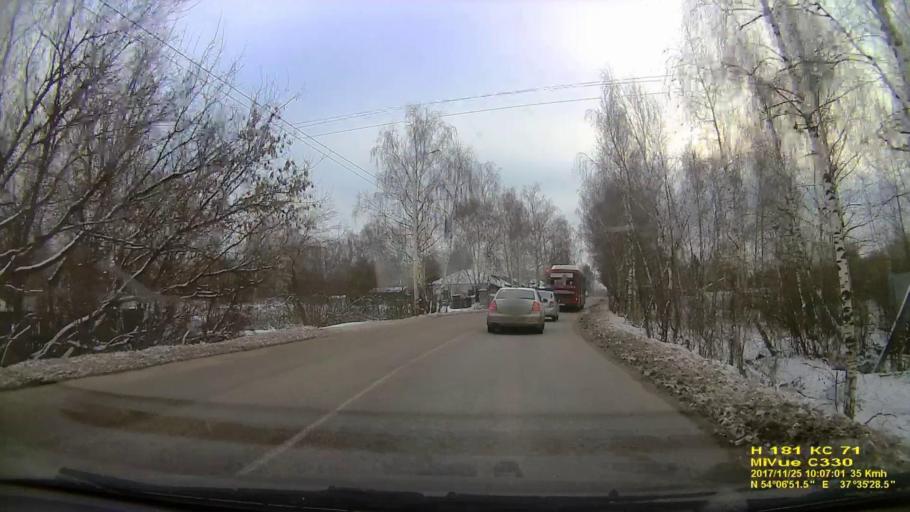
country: RU
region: Tula
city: Skuratovskiy
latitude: 54.1143
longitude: 37.5914
